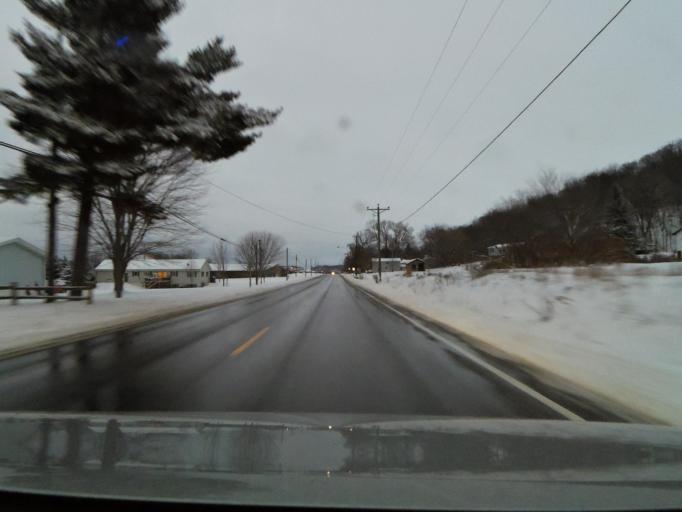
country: US
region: Wisconsin
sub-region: Dunn County
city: Boyceville
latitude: 44.9553
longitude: -92.0724
